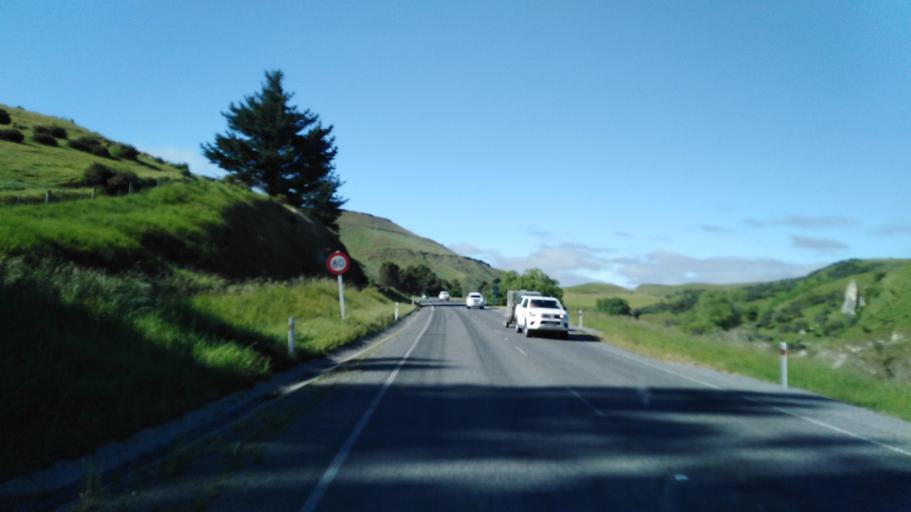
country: NZ
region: Canterbury
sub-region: Hurunui District
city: Amberley
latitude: -42.9883
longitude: 172.7208
